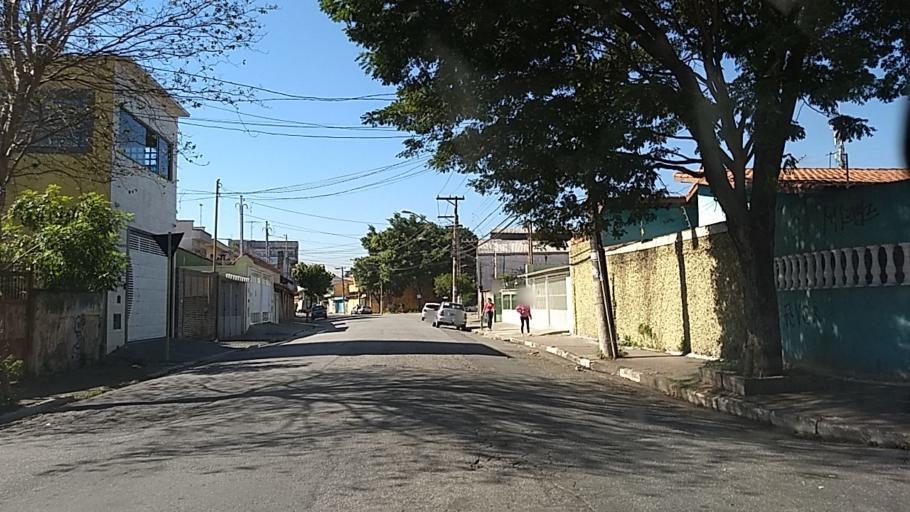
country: BR
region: Sao Paulo
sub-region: Guarulhos
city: Guarulhos
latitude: -23.4802
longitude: -46.5657
